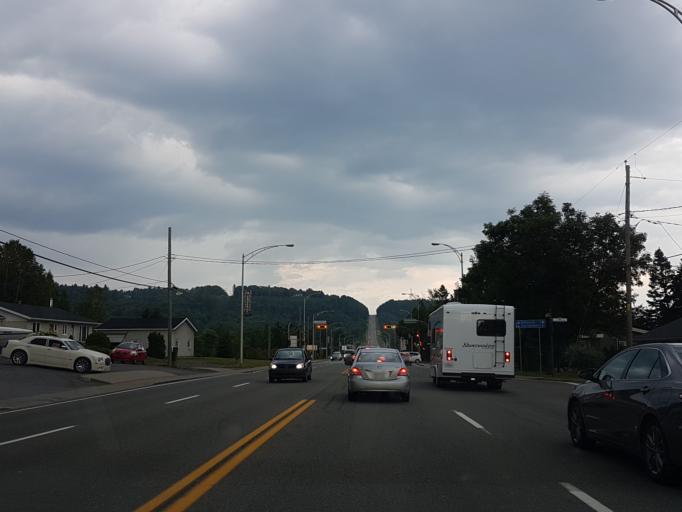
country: CA
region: Quebec
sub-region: Capitale-Nationale
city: Beaupre
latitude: 47.0484
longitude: -70.8891
